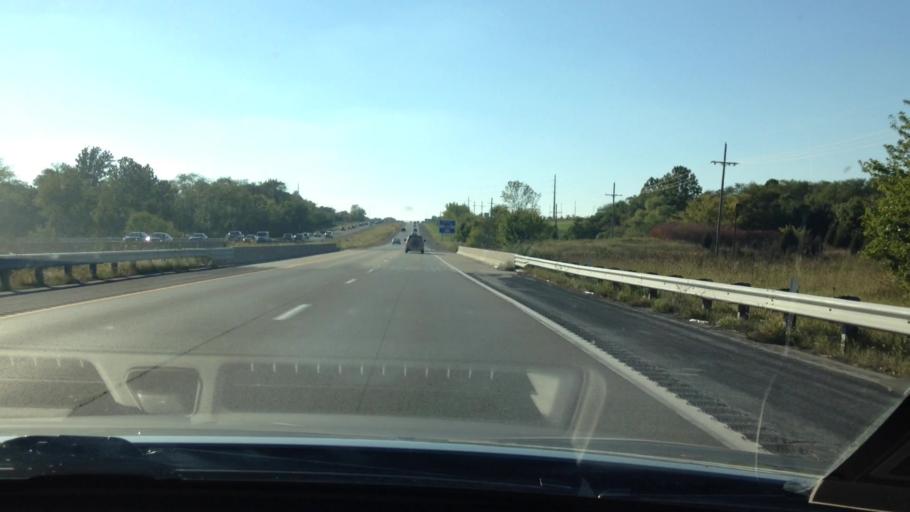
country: US
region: Missouri
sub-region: Platte County
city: Riverside
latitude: 39.2542
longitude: -94.6162
